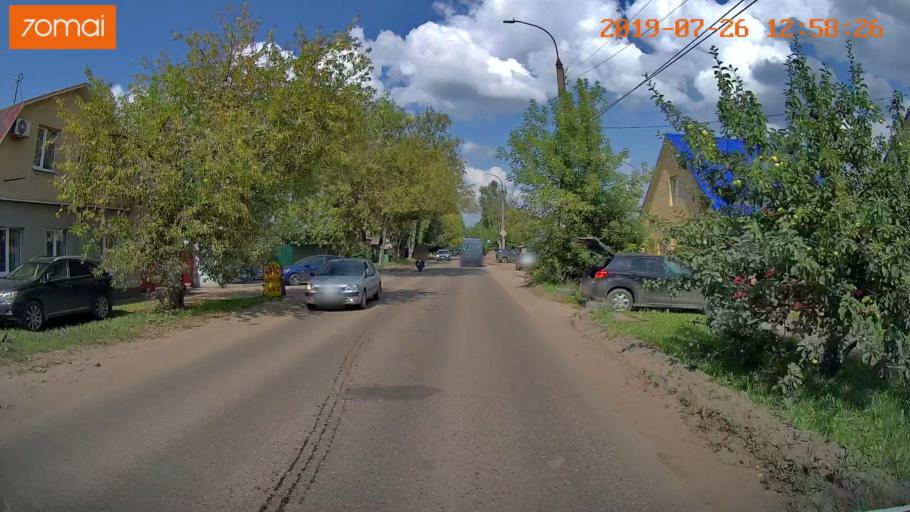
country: RU
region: Ivanovo
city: Bogorodskoye
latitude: 57.0241
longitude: 41.0208
